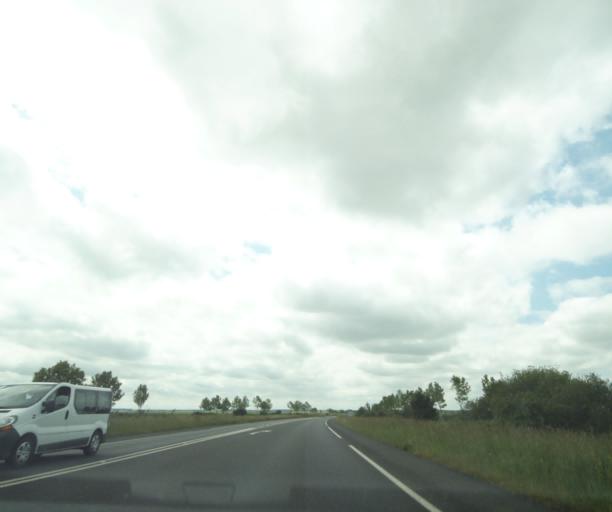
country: FR
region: Poitou-Charentes
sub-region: Departement des Deux-Sevres
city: Saint-Varent
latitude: 46.9046
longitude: -0.1910
